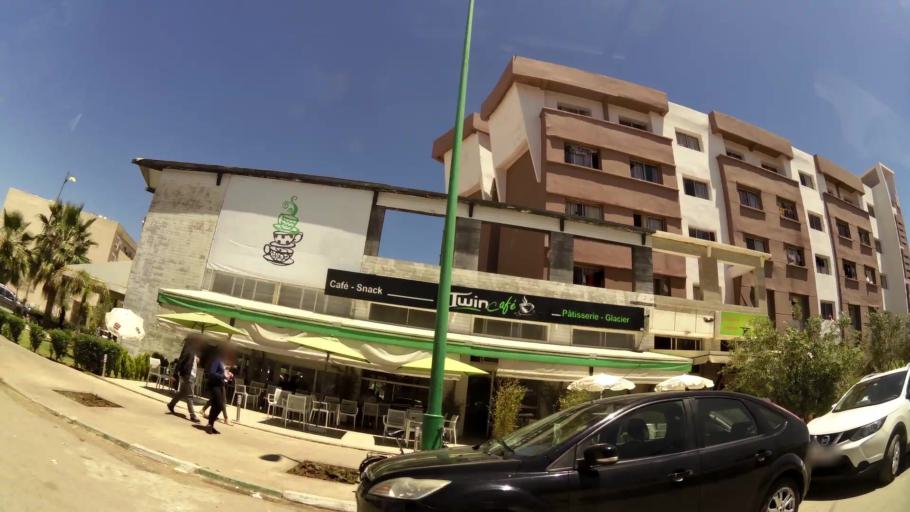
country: MA
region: Meknes-Tafilalet
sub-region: Meknes
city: Meknes
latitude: 33.8585
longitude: -5.5709
